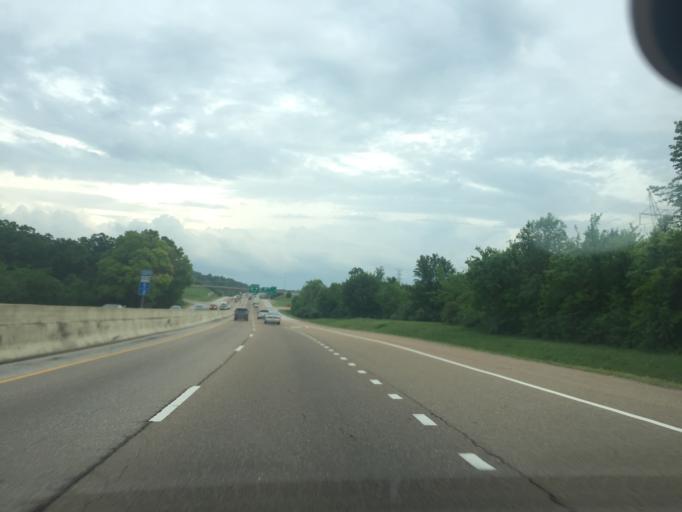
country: US
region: Tennessee
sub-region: Hamilton County
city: East Chattanooga
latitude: 35.0928
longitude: -85.2232
